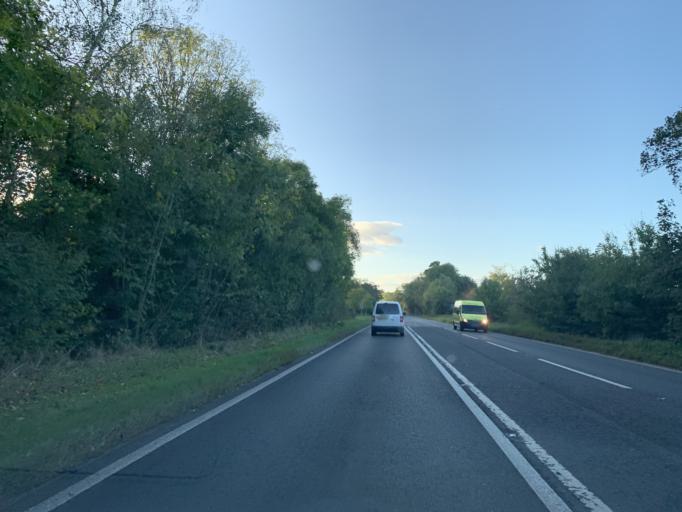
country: GB
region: England
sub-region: Wiltshire
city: Whiteparish
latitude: 50.9775
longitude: -1.6287
